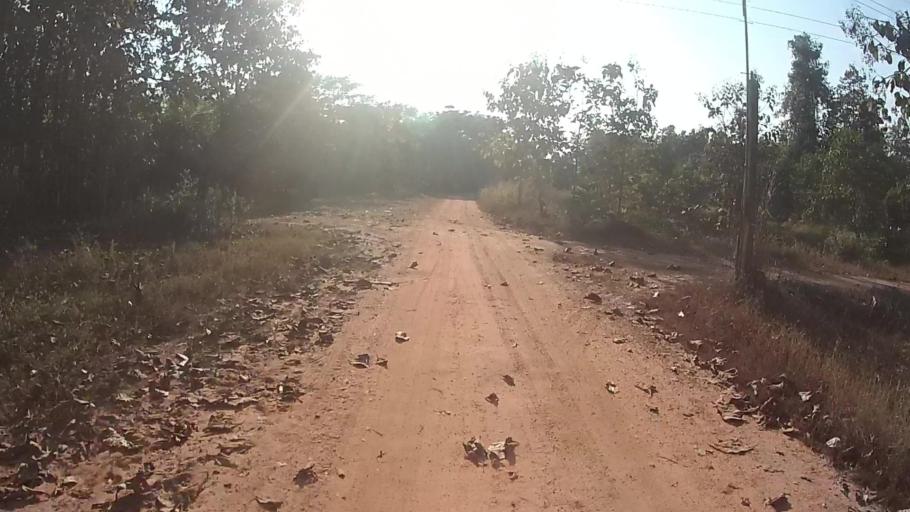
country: TH
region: Chiang Mai
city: San Sai
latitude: 18.9107
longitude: 99.0571
